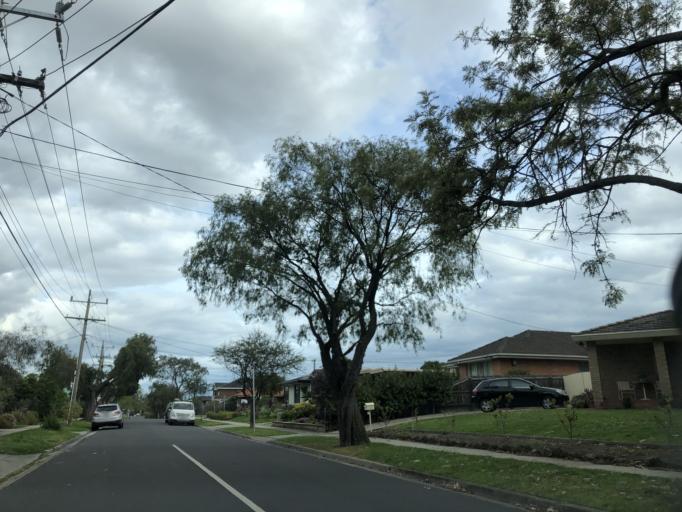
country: AU
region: Victoria
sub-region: Monash
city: Oakleigh South
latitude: -37.9217
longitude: 145.0923
